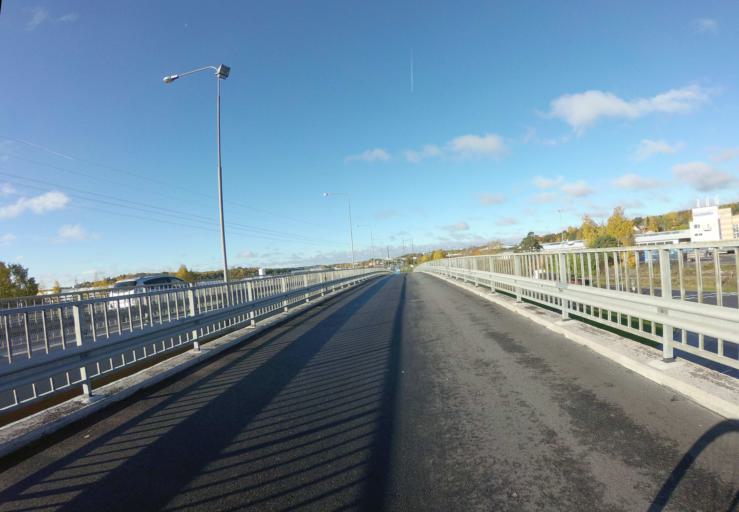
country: FI
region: Varsinais-Suomi
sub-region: Turku
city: Turku
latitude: 60.4480
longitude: 22.2163
